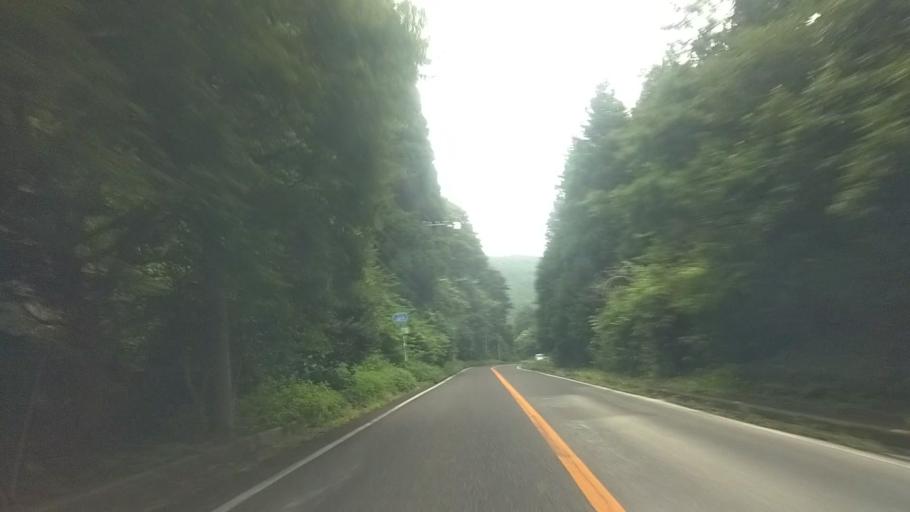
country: JP
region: Chiba
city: Katsuura
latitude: 35.2447
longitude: 140.1883
